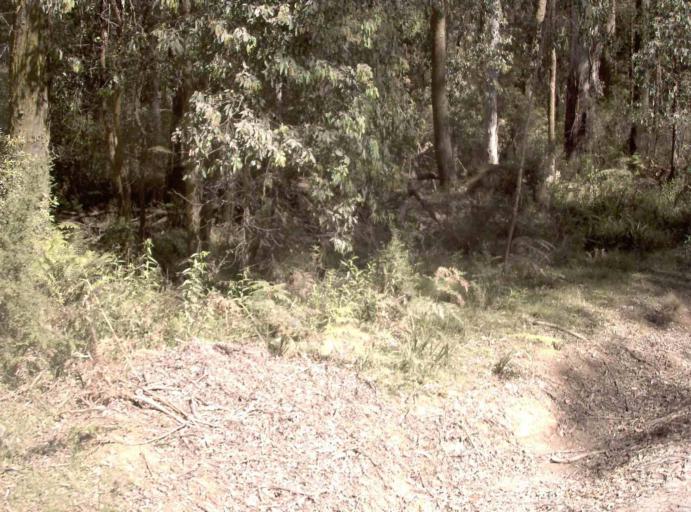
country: AU
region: New South Wales
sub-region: Bombala
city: Bombala
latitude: -37.2060
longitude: 148.7313
